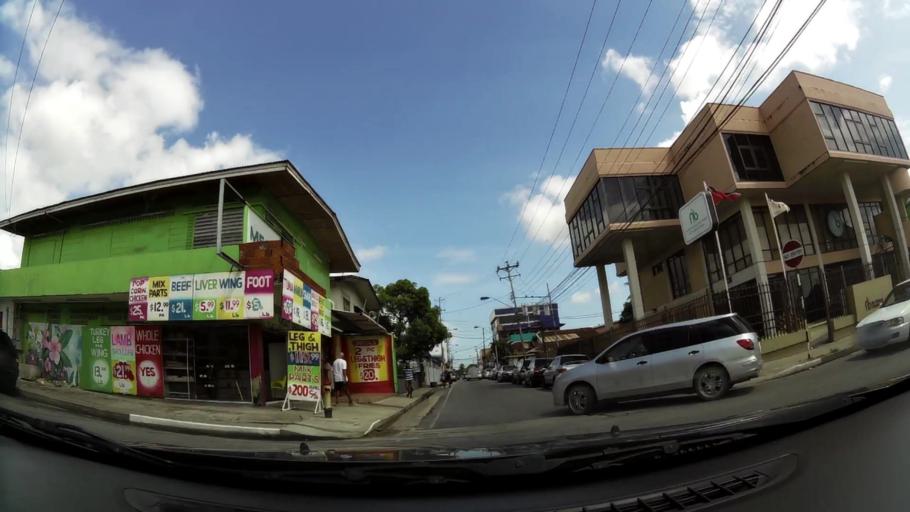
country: TT
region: Borough of Arima
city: Arima
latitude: 10.6422
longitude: -61.2830
